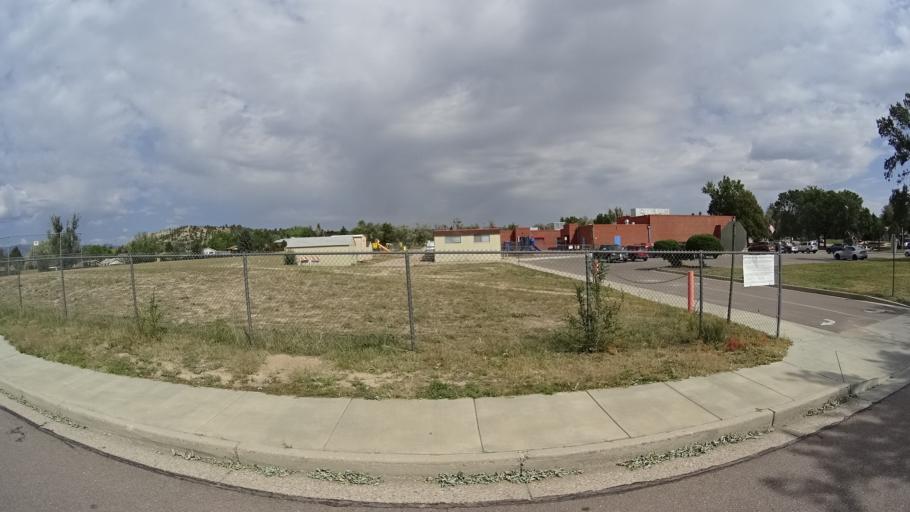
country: US
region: Colorado
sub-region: El Paso County
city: Cimarron Hills
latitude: 38.8505
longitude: -104.7338
